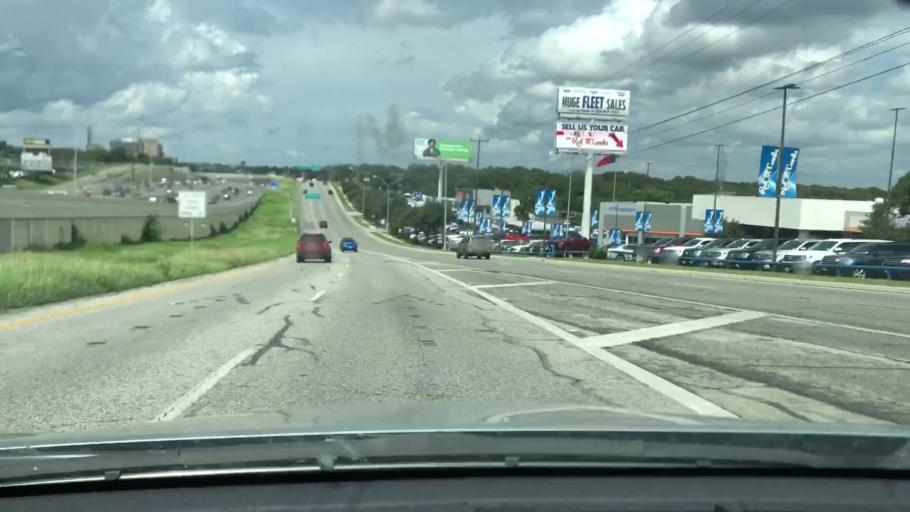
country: US
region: Texas
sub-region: Bexar County
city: Balcones Heights
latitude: 29.5165
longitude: -98.5534
